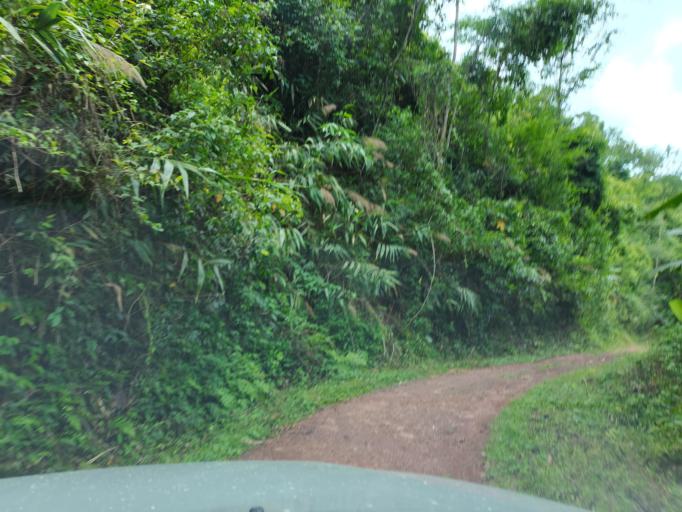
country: LA
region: Loungnamtha
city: Muang Nale
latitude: 20.5111
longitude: 101.0799
